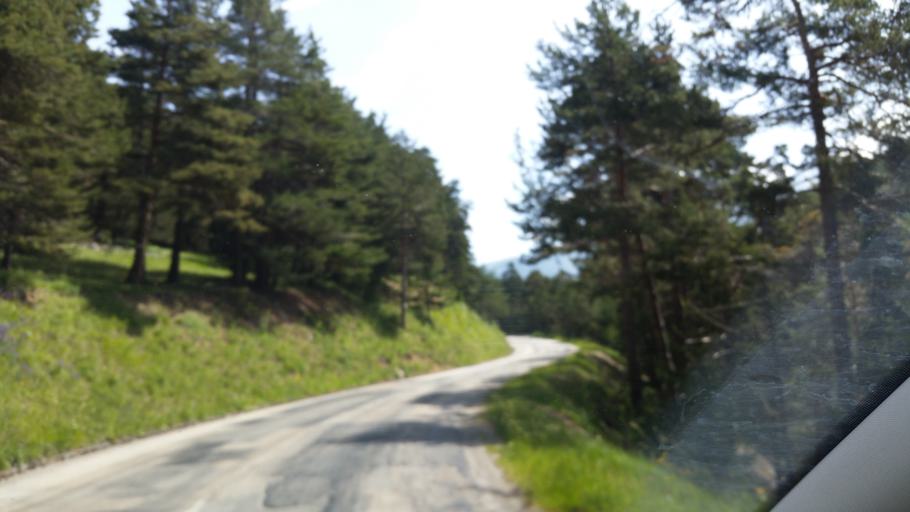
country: FR
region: Rhone-Alpes
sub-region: Departement de la Savoie
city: Modane
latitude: 45.2380
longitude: 6.7681
